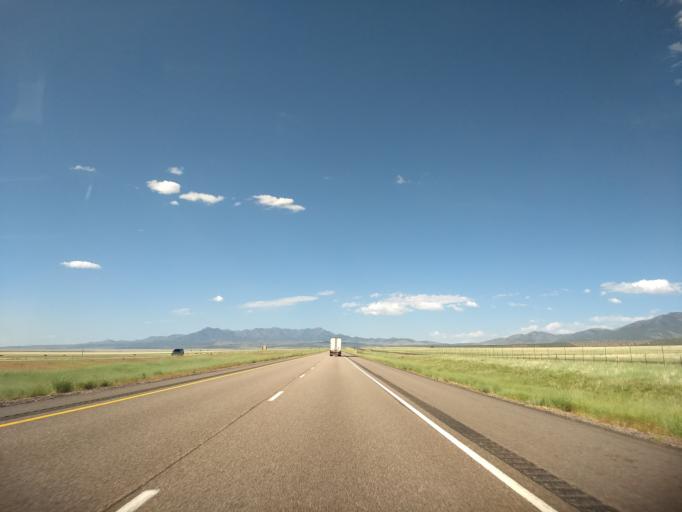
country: US
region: Utah
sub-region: Millard County
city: Fillmore
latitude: 39.0324
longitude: -112.2984
